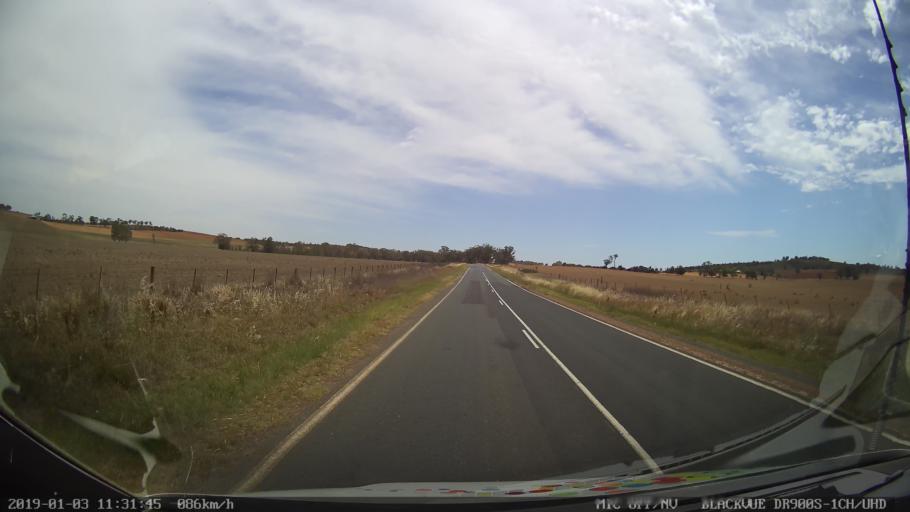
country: AU
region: New South Wales
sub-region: Weddin
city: Grenfell
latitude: -33.9669
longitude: 148.1818
